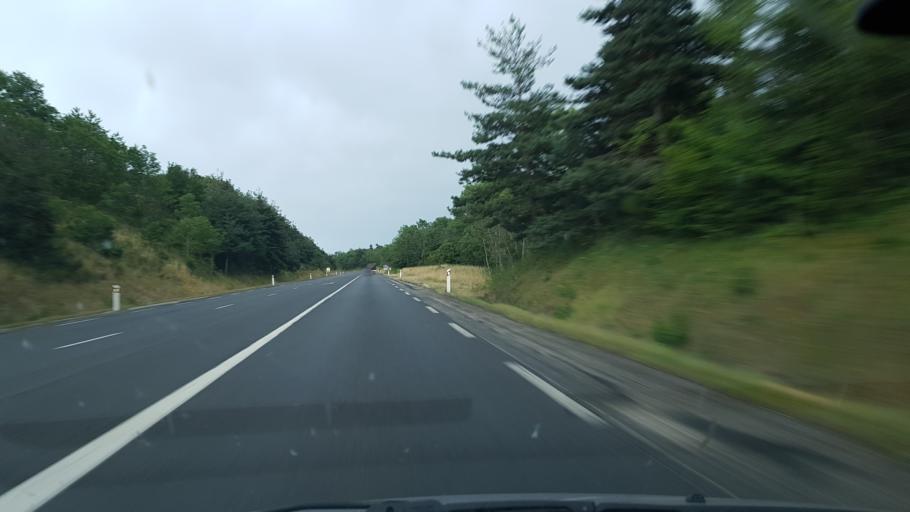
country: FR
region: Auvergne
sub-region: Departement de la Haute-Loire
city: Allegre
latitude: 45.1374
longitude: 3.6131
